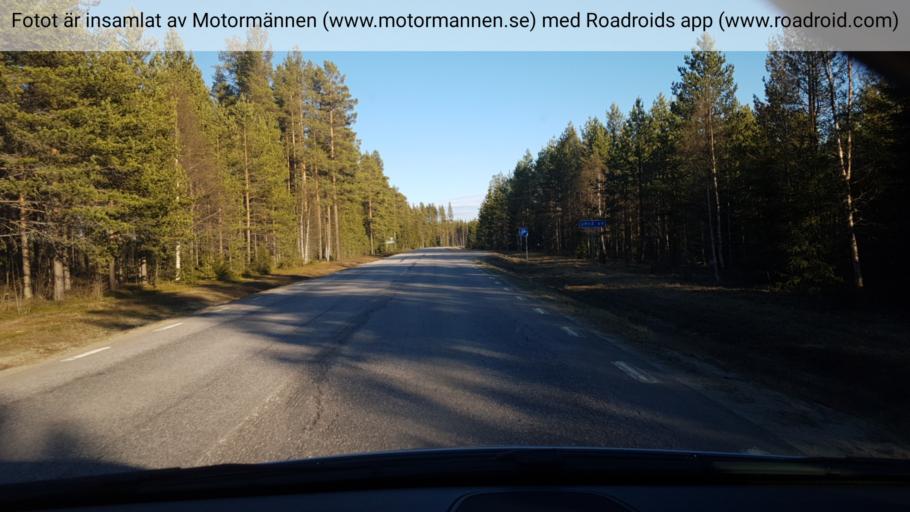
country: SE
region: Vaesterbotten
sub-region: Vindelns Kommun
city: Vindeln
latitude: 64.0837
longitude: 19.6283
